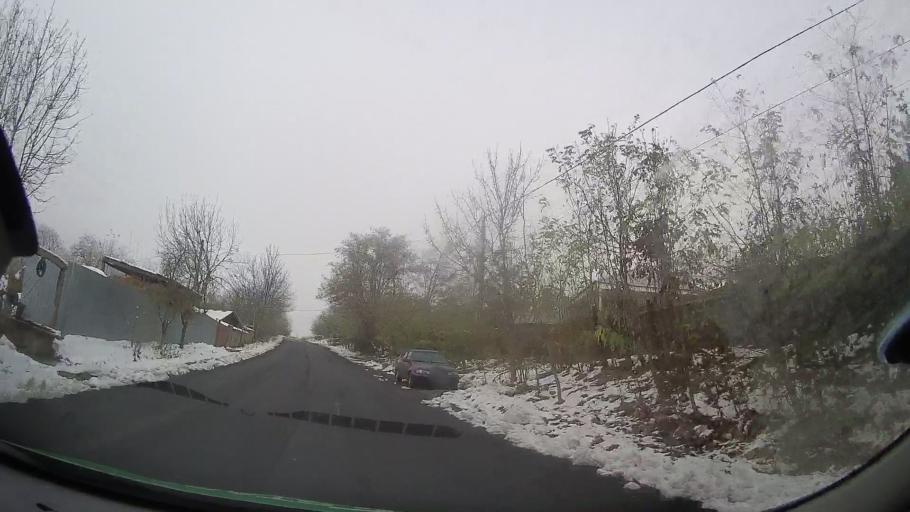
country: RO
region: Vaslui
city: Coroiesti
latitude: 46.2123
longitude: 27.4415
